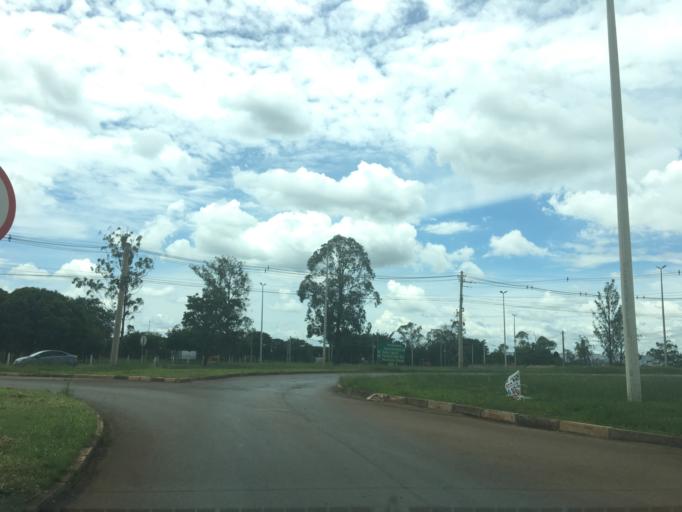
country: BR
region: Federal District
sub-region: Brasilia
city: Brasilia
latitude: -15.8325
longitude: -47.9418
